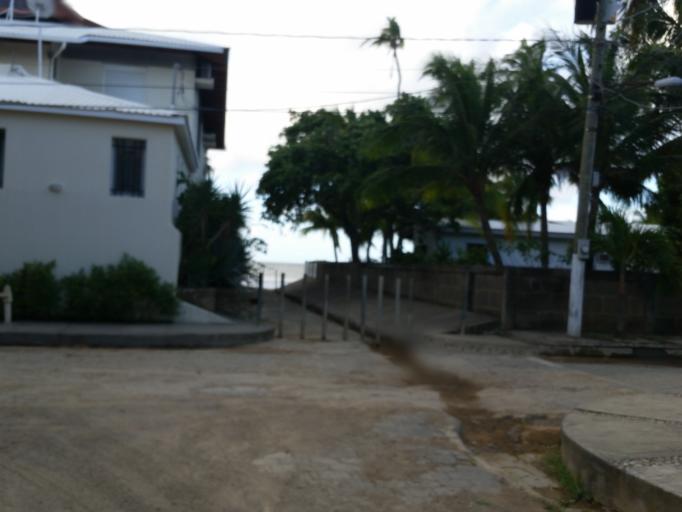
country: NI
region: Rivas
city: San Juan del Sur
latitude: 11.2615
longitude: -85.8772
